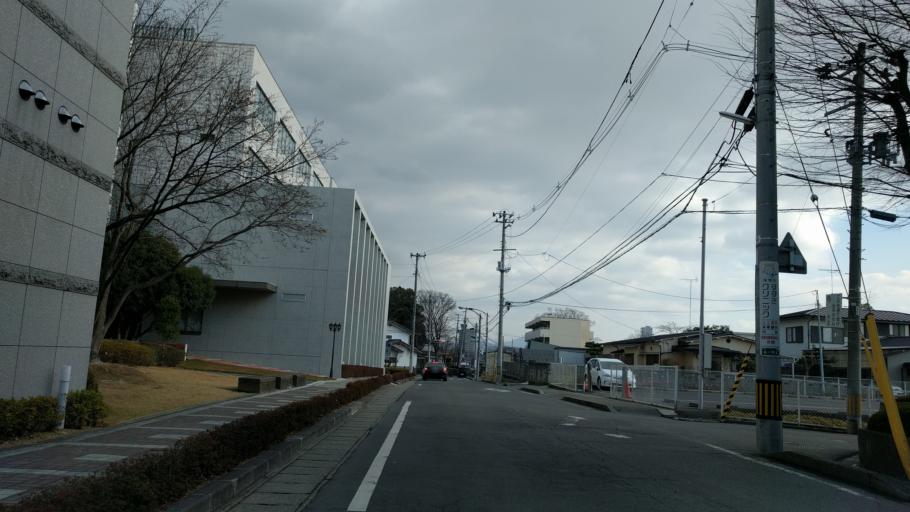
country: JP
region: Fukushima
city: Koriyama
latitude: 37.4068
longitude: 140.3665
